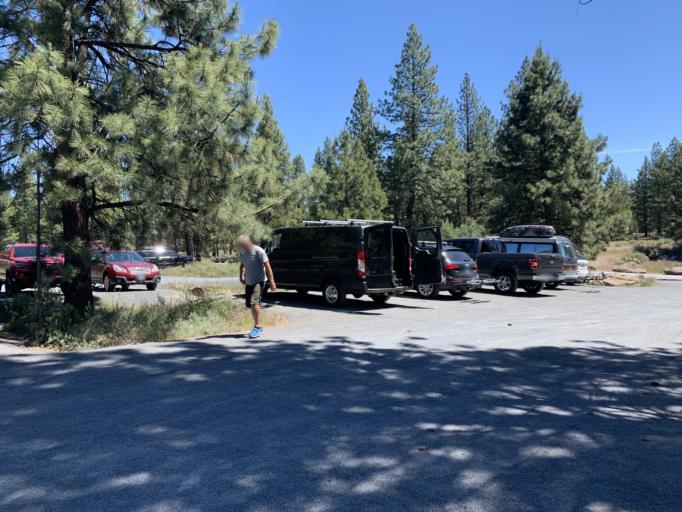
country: US
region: Oregon
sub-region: Deschutes County
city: Deschutes River Woods
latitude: 44.0434
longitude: -121.3859
